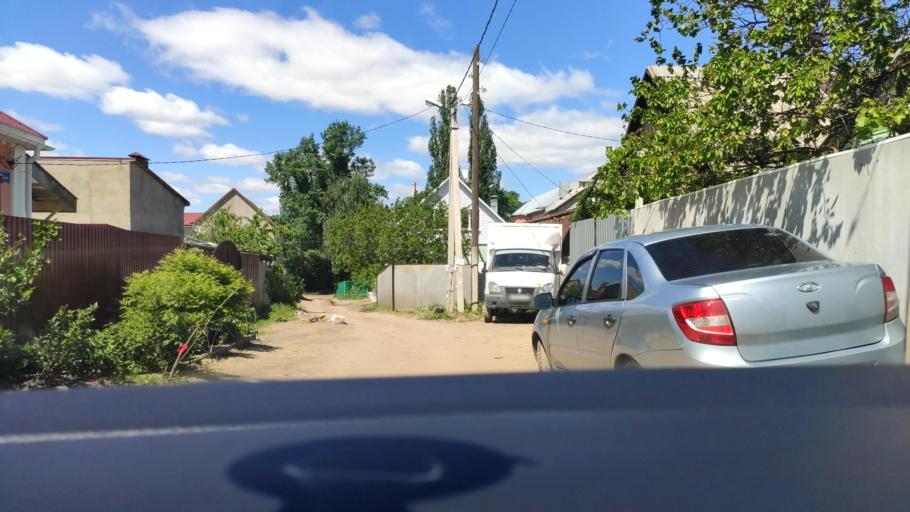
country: RU
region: Voronezj
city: Maslovka
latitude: 51.6158
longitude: 39.2331
